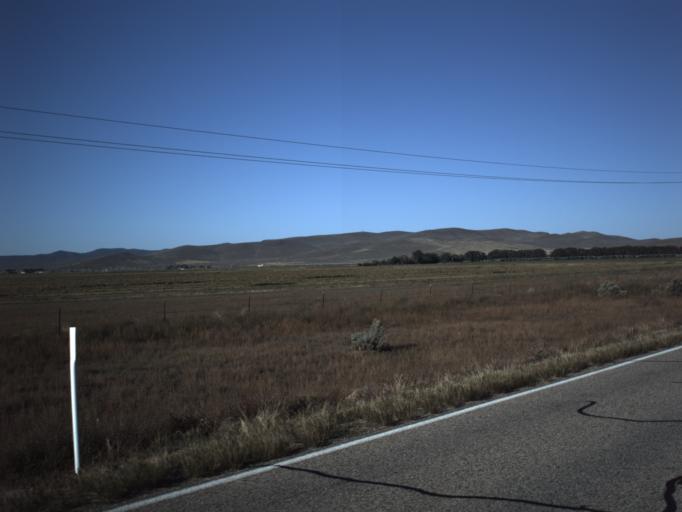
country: US
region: Utah
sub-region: Washington County
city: Enterprise
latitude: 37.7163
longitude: -113.6751
